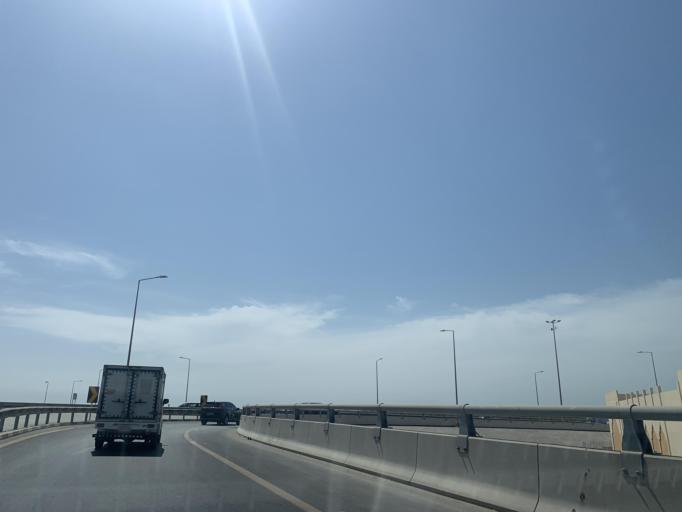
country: BH
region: Central Governorate
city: Madinat Hamad
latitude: 26.1747
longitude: 50.4664
